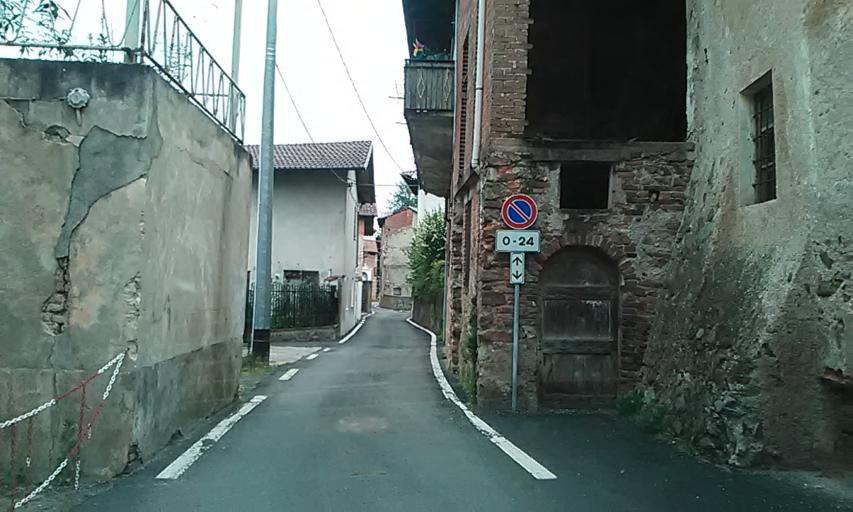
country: IT
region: Piedmont
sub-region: Provincia di Biella
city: Villa del Bosco
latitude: 45.6267
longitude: 8.2748
